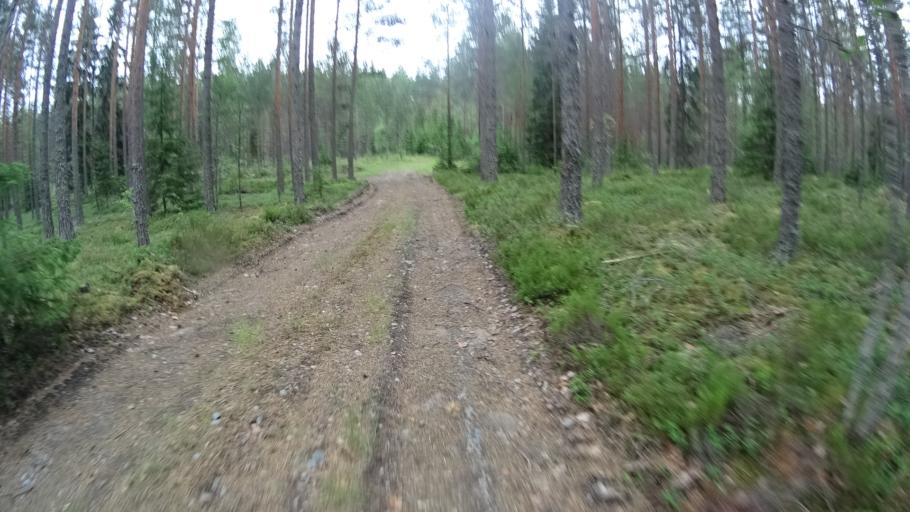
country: FI
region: Uusimaa
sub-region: Helsinki
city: Karkkila
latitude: 60.6024
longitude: 24.1586
